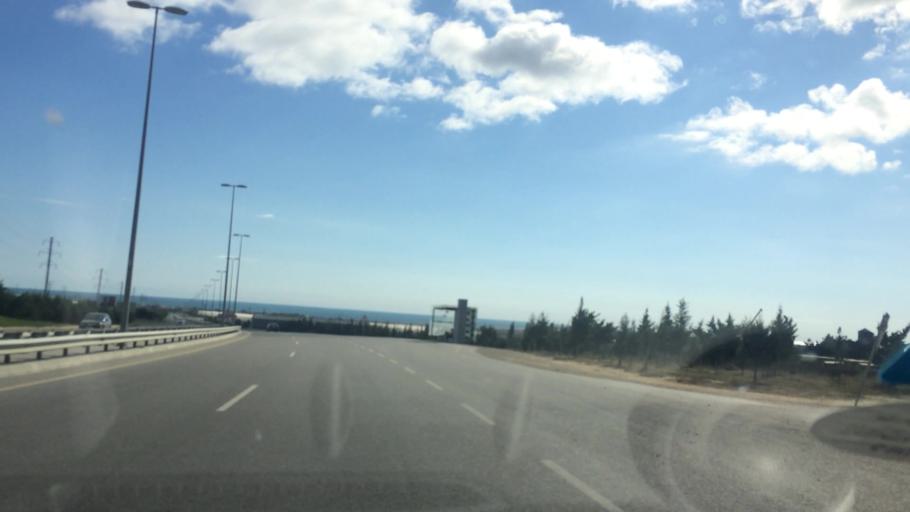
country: AZ
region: Baki
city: Zyrya
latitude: 40.4013
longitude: 50.3104
